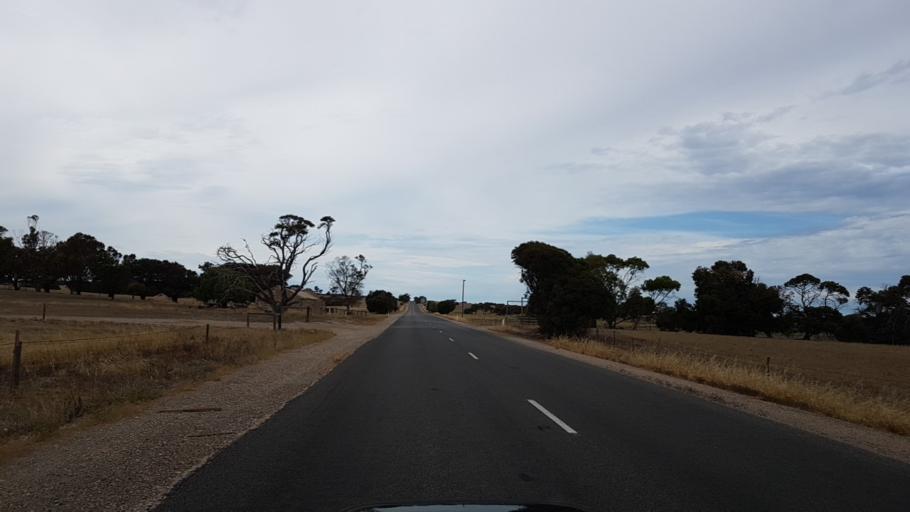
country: AU
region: South Australia
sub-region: Yorke Peninsula
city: Honiton
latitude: -34.9391
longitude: 137.0920
